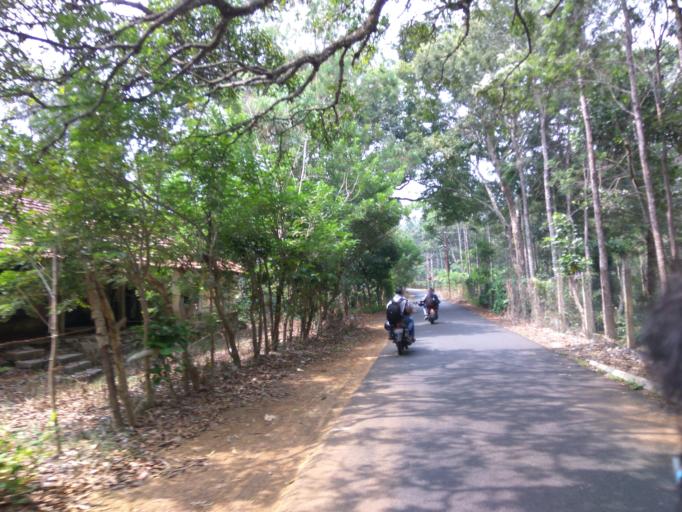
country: IN
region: Tamil Nadu
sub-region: Salem
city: Salem
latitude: 11.7754
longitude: 78.2202
